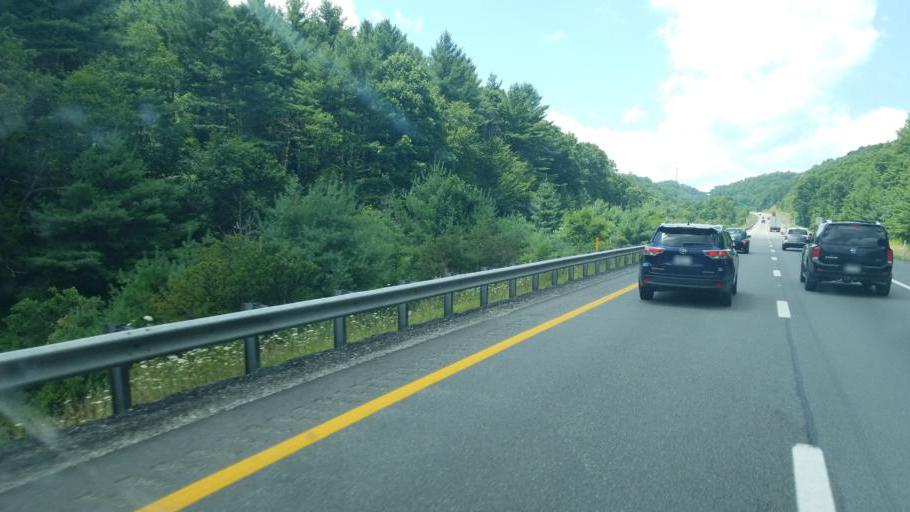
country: US
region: West Virginia
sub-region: Raleigh County
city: Beaver
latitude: 37.7188
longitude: -81.1643
